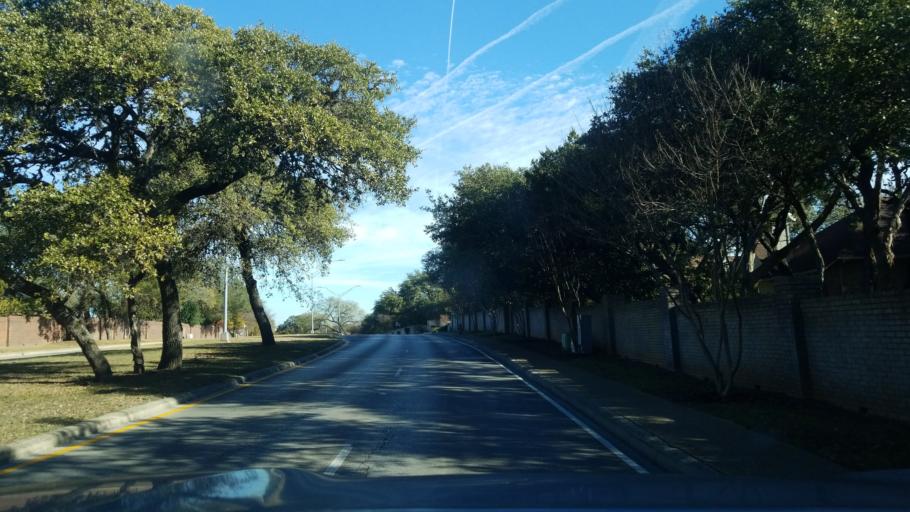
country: US
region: Texas
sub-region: Bexar County
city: Shavano Park
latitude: 29.5992
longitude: -98.5238
